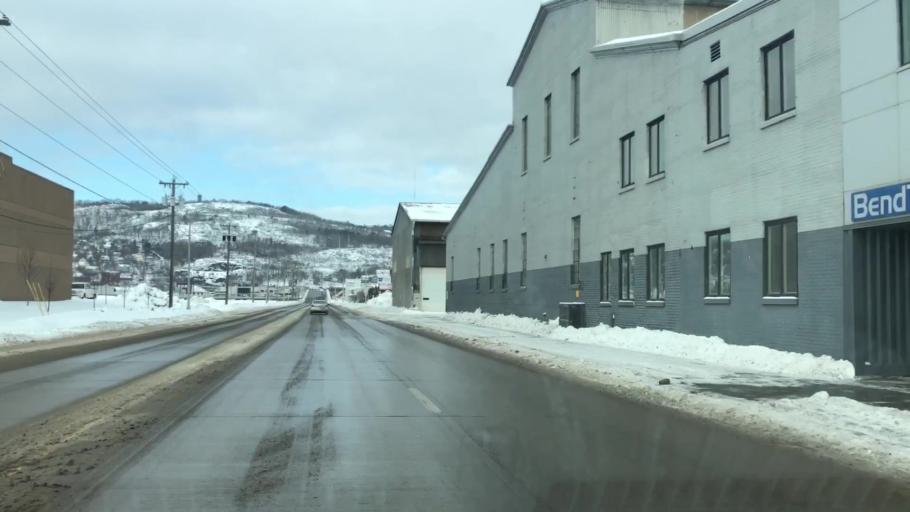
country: US
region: Minnesota
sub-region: Saint Louis County
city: Duluth
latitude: 46.7641
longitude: -92.1125
